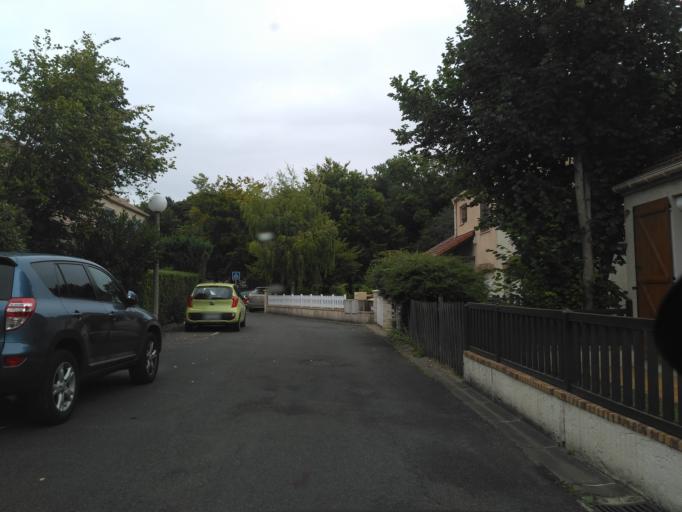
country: FR
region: Ile-de-France
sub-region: Departement de Seine-et-Marne
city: Vert-Saint-Denis
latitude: 48.5634
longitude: 2.6274
